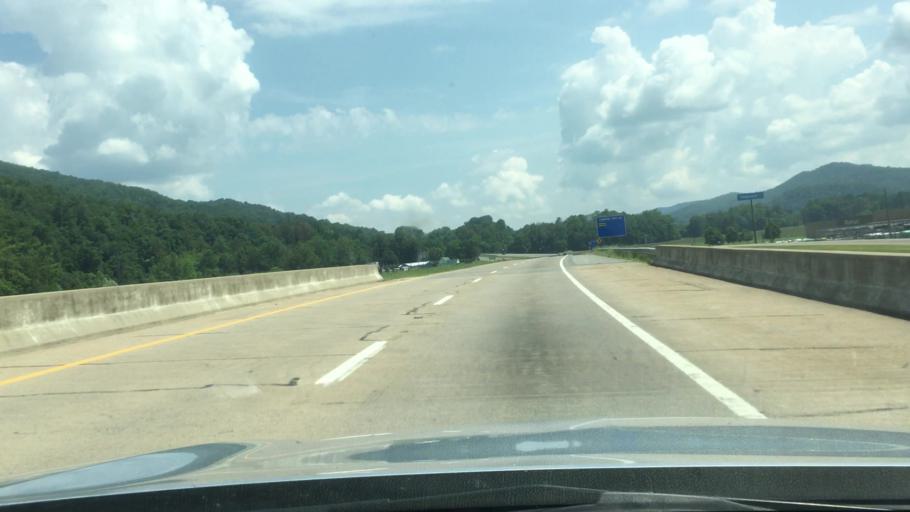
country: US
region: Tennessee
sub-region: Unicoi County
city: Unicoi
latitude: 36.1876
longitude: -82.3765
